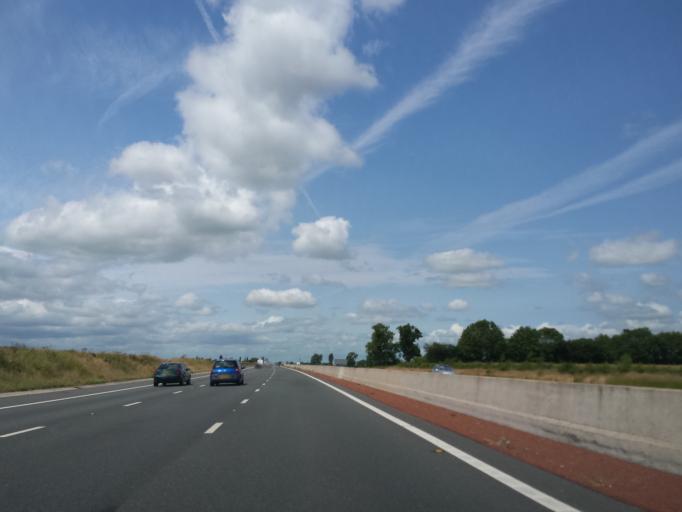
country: GB
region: England
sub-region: North Yorkshire
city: Ripon
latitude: 54.2050
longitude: -1.4738
